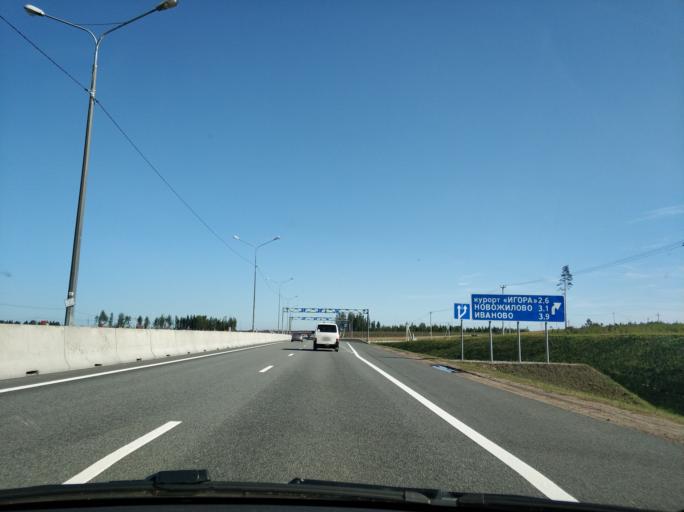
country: RU
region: Leningrad
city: Sosnovo
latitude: 60.4986
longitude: 30.1958
